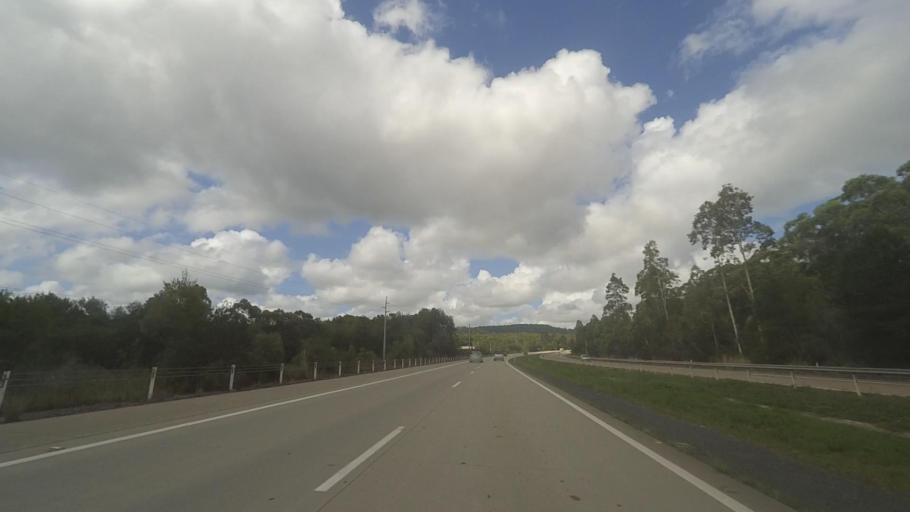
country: AU
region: New South Wales
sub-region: Great Lakes
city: Bulahdelah
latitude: -32.3880
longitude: 152.2259
